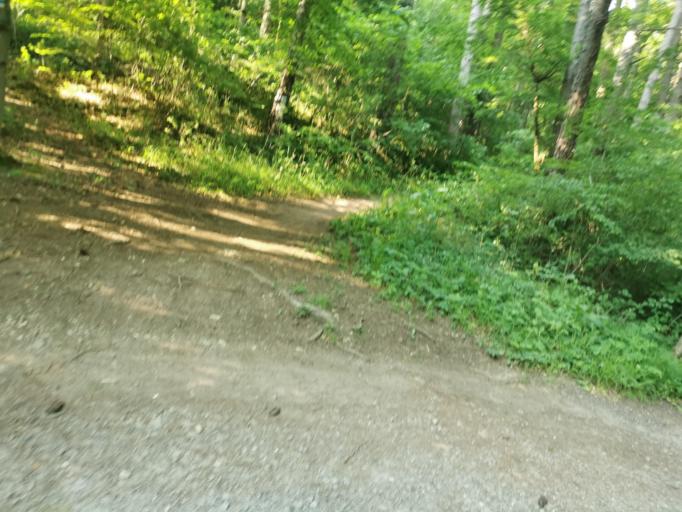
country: CZ
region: South Moravian
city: Knezdub
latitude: 48.8574
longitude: 17.3755
